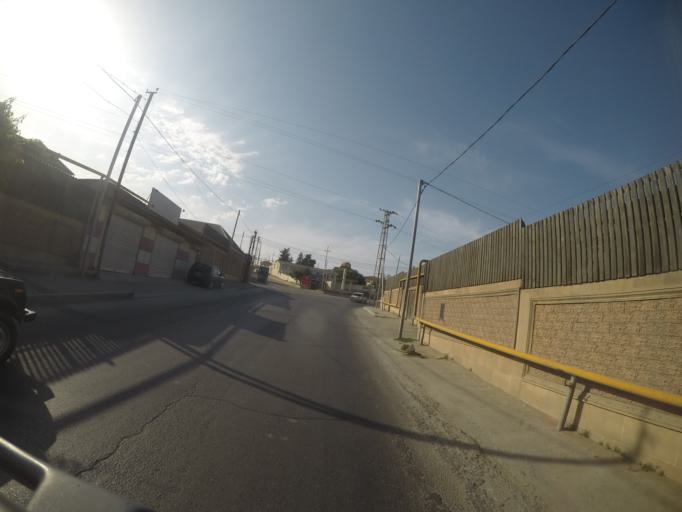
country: AZ
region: Baki
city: Binagadi
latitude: 40.4650
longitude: 49.8420
